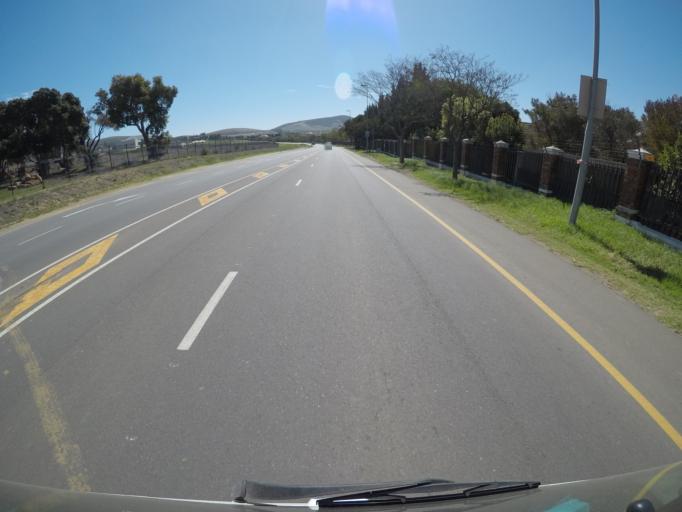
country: ZA
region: Western Cape
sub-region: City of Cape Town
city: Kraaifontein
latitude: -33.8176
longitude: 18.6344
